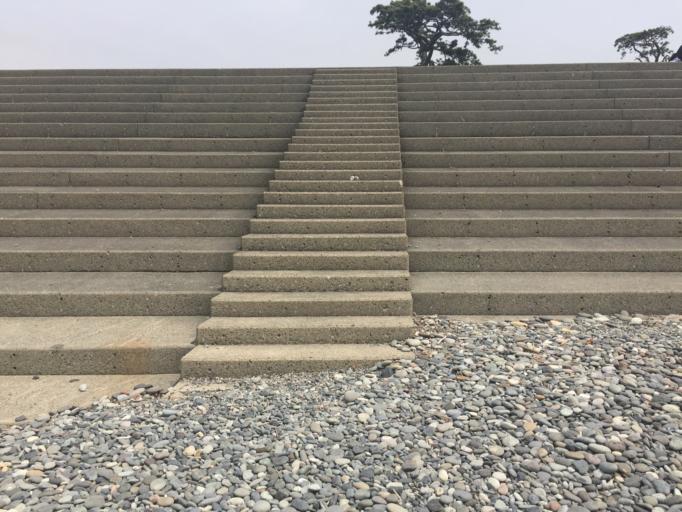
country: JP
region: Shizuoka
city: Numazu
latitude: 35.0915
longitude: 138.8481
